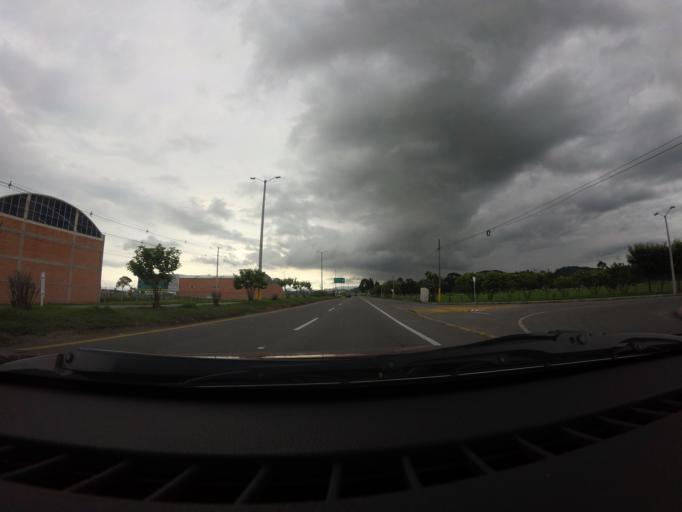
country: CO
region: Cundinamarca
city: Funza
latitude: 4.7842
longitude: -74.1899
